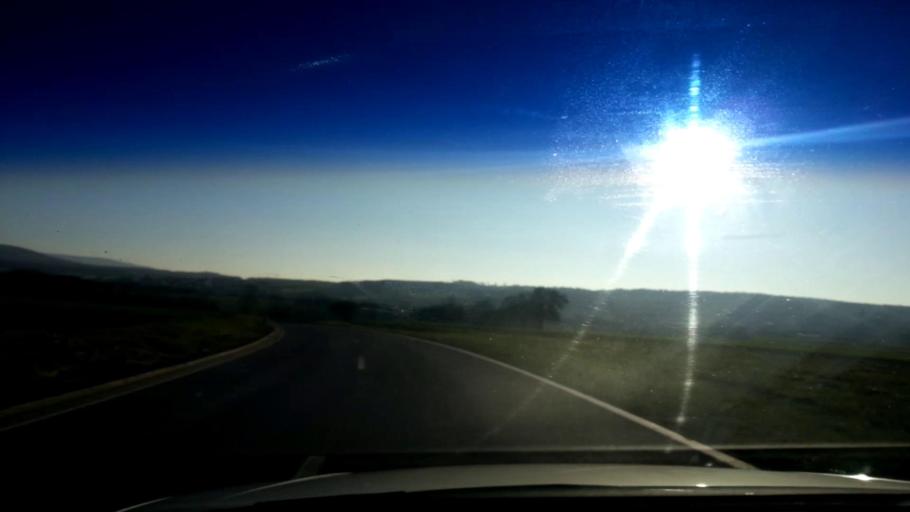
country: DE
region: Bavaria
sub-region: Upper Franconia
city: Litzendorf
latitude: 49.9200
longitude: 10.9973
